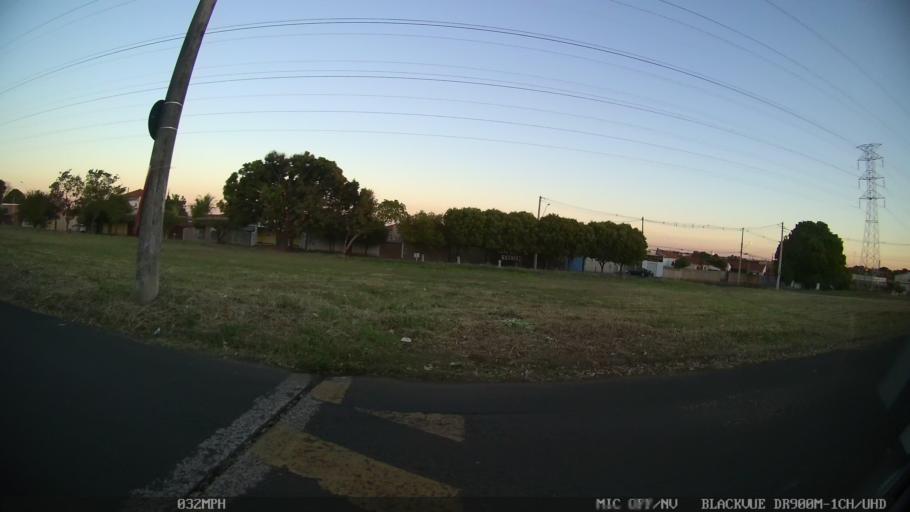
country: BR
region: Sao Paulo
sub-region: Sao Jose Do Rio Preto
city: Sao Jose do Rio Preto
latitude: -20.8429
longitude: -49.3766
